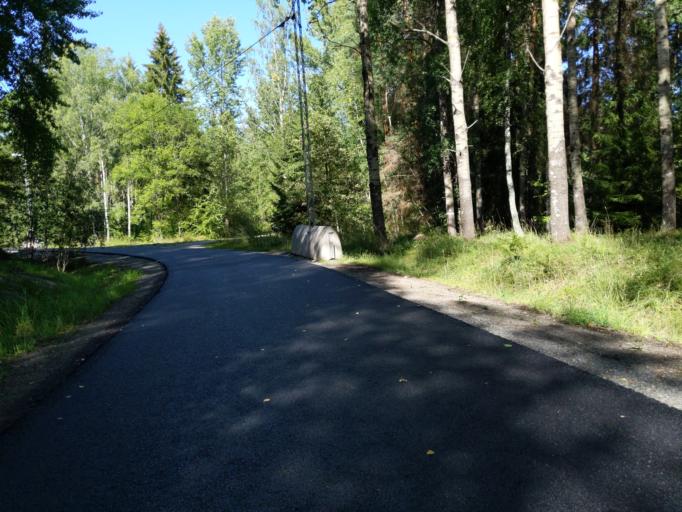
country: SE
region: Stockholm
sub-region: Stockholms Kommun
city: Kista
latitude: 59.3885
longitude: 17.9591
